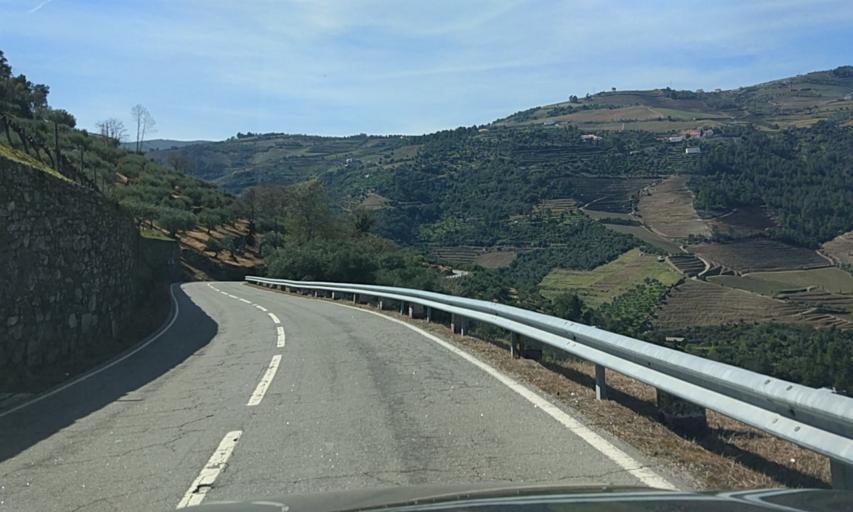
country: PT
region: Vila Real
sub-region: Sabrosa
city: Sabrosa
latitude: 41.2184
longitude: -7.5353
